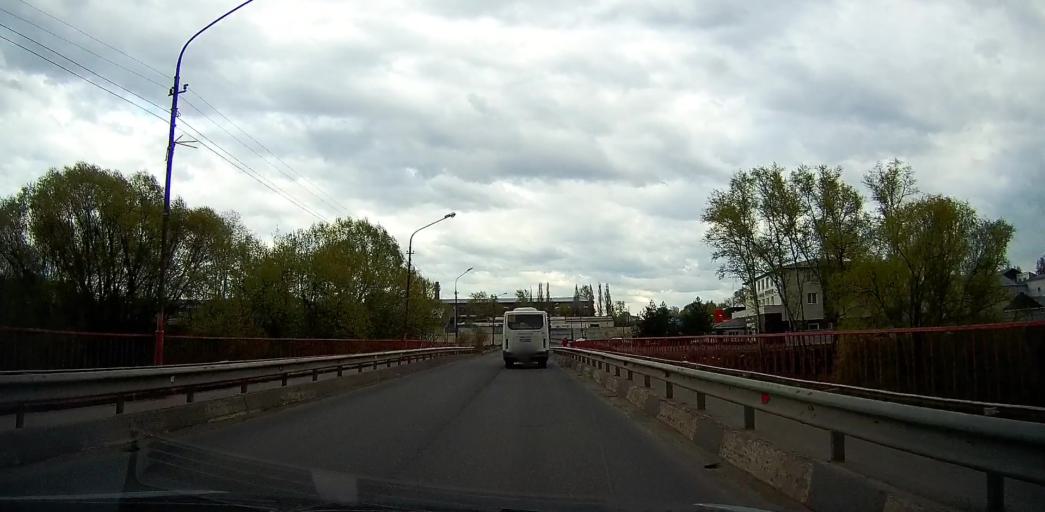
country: RU
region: Moskovskaya
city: Pavlovskiy Posad
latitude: 55.7798
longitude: 38.6876
